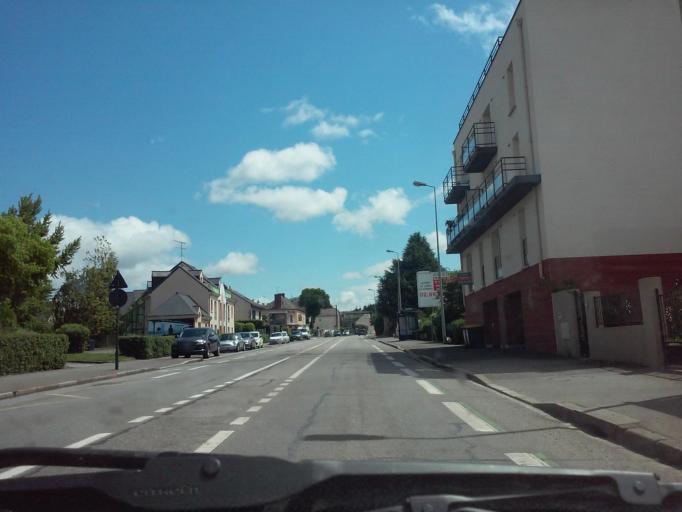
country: FR
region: Brittany
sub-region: Departement d'Ille-et-Vilaine
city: Rennes
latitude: 48.0994
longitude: -1.6468
